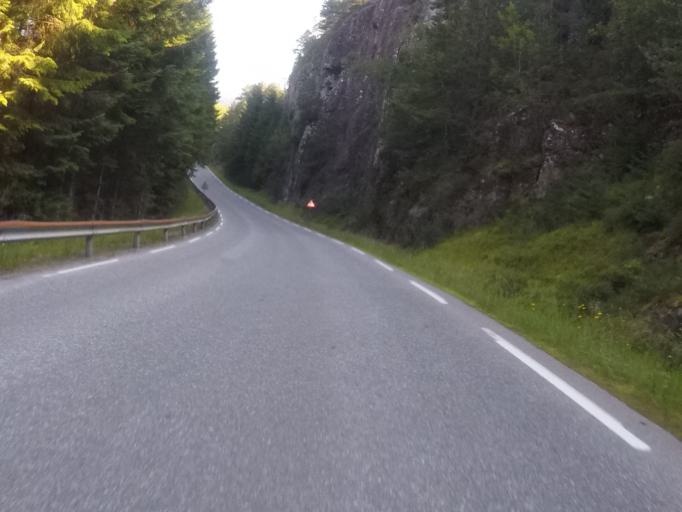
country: NO
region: Sogn og Fjordane
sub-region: Bremanger
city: Svelgen
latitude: 61.7214
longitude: 5.2036
